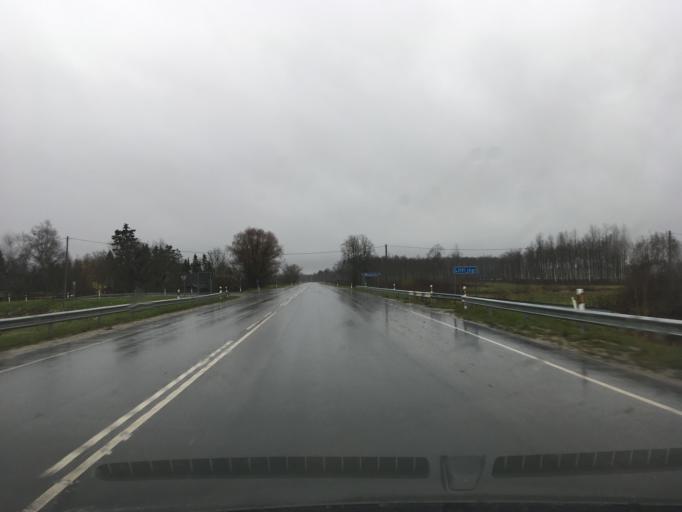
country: EE
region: Harju
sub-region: Nissi vald
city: Turba
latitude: 58.8612
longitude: 24.0745
